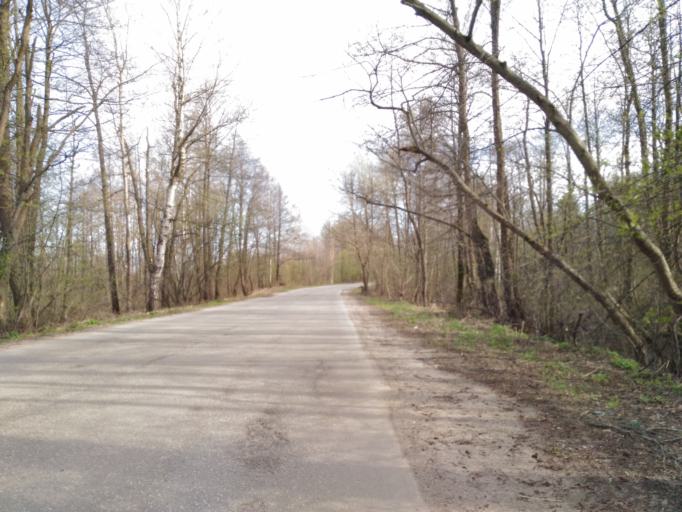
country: RU
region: Vladimir
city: Petushki
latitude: 55.9138
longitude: 39.4658
